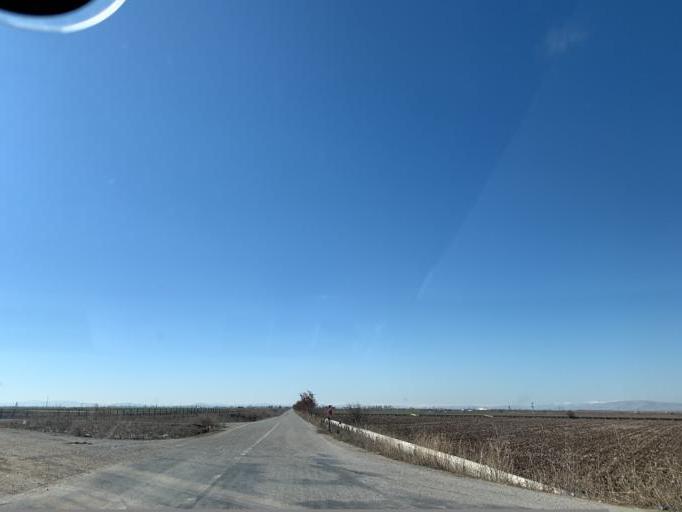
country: TR
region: Konya
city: Catalhoeyuek
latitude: 37.6288
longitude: 32.8082
